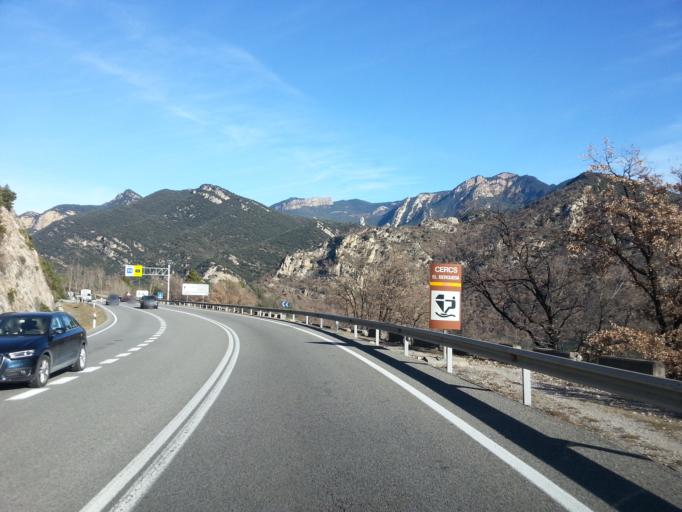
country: ES
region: Catalonia
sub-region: Provincia de Barcelona
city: Berga
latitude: 42.1388
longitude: 1.8651
